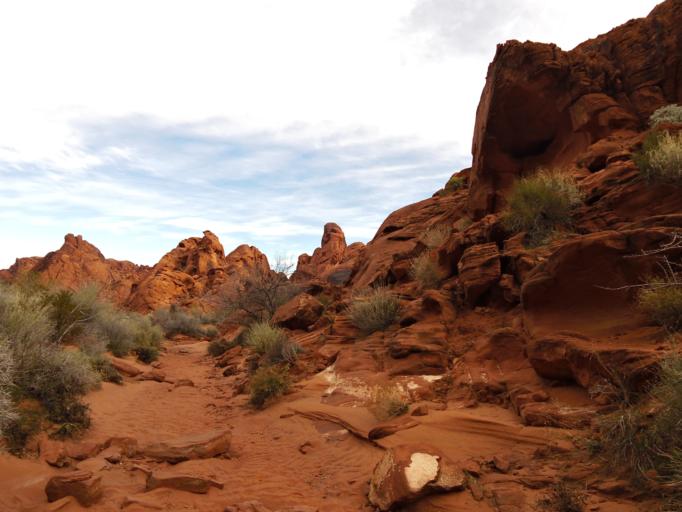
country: US
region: Nevada
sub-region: Clark County
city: Moapa Valley
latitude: 36.4392
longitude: -114.5146
